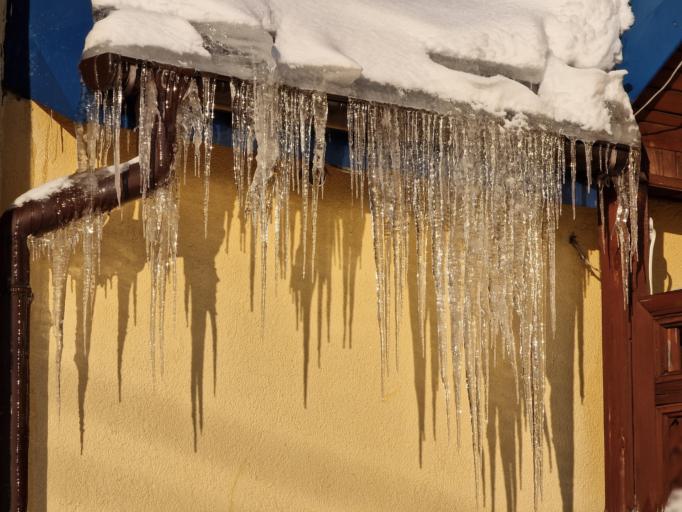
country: PL
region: Silesian Voivodeship
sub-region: Powiat bedzinski
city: Saczow
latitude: 50.4485
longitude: 19.0207
